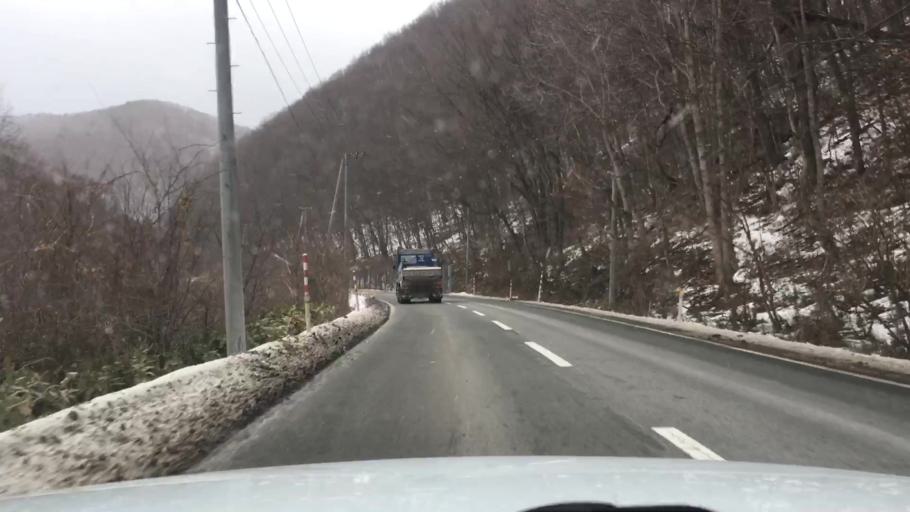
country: JP
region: Iwate
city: Tono
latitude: 39.6268
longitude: 141.4662
